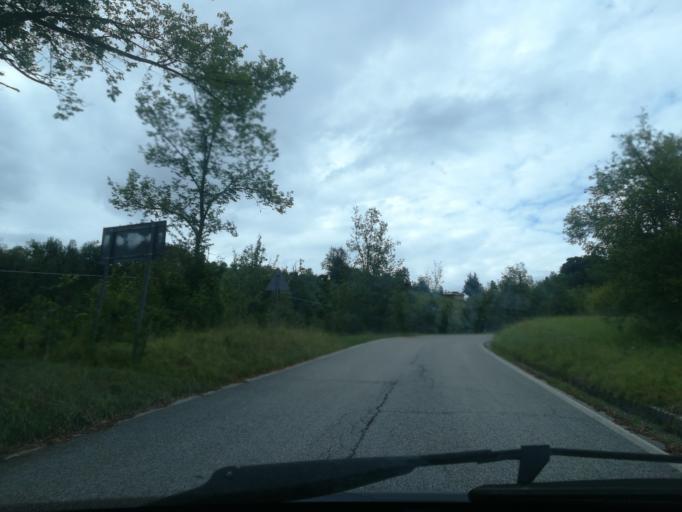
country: IT
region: The Marches
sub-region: Province of Fermo
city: Montefortino
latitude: 42.9383
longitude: 13.3727
